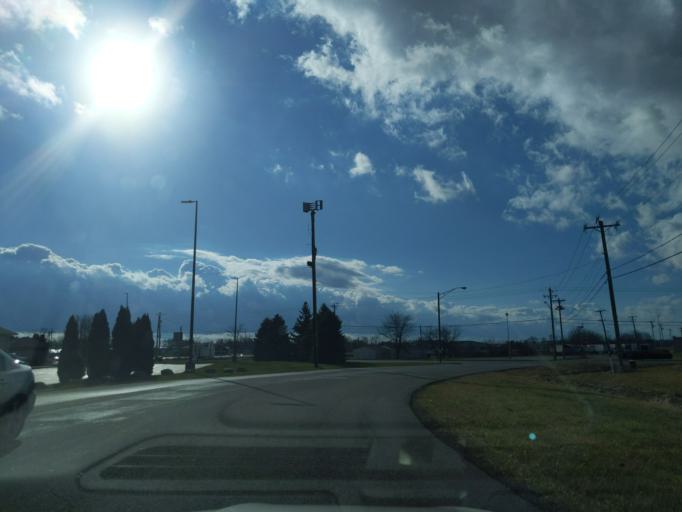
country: US
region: Indiana
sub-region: Decatur County
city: Greensburg
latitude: 39.3498
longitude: -85.4989
